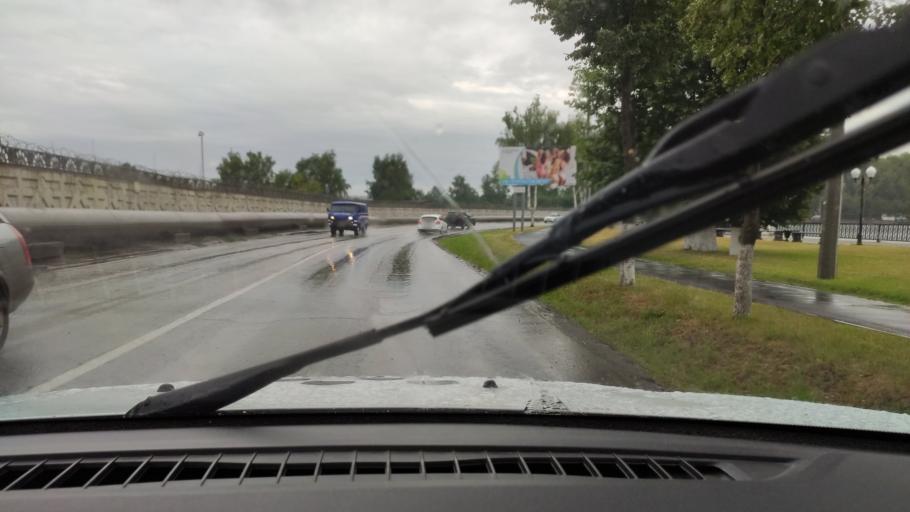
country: RU
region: Udmurtiya
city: Votkinsk
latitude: 57.0511
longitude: 53.9769
